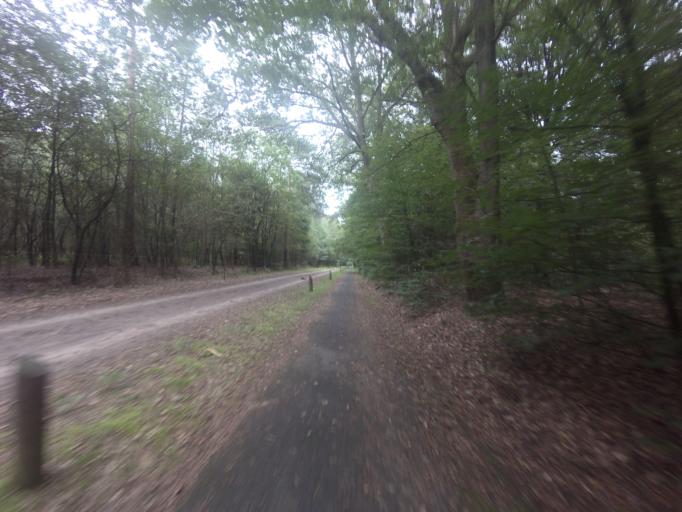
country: NL
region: Drenthe
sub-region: Gemeente Westerveld
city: Dwingeloo
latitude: 52.8778
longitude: 6.2725
